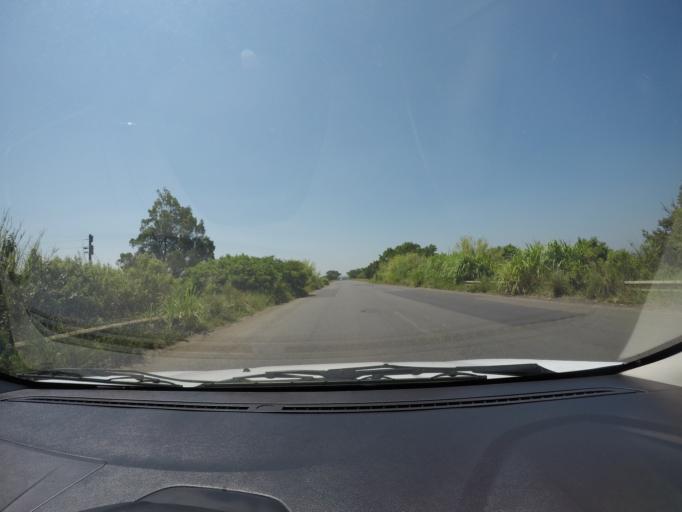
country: ZA
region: KwaZulu-Natal
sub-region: uThungulu District Municipality
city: Empangeni
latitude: -28.8010
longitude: 31.9584
